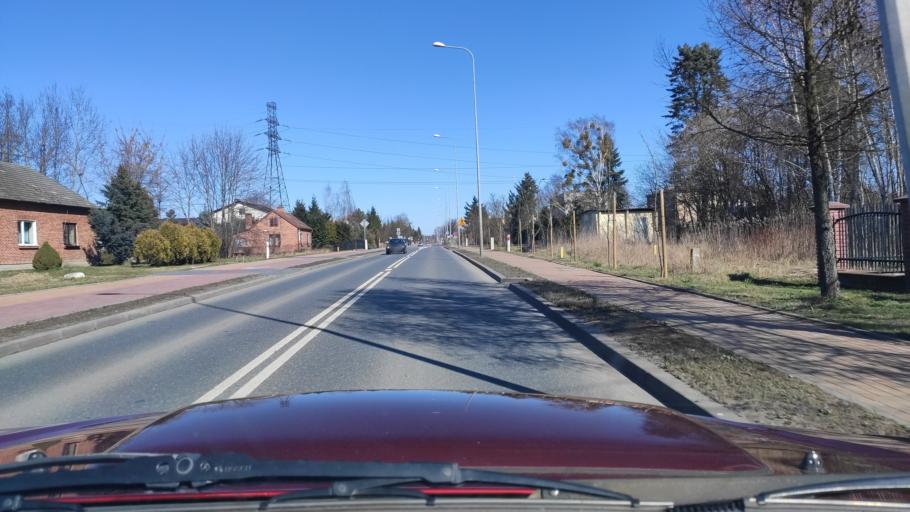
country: PL
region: Masovian Voivodeship
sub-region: Powiat zwolenski
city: Zwolen
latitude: 51.3675
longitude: 21.5853
